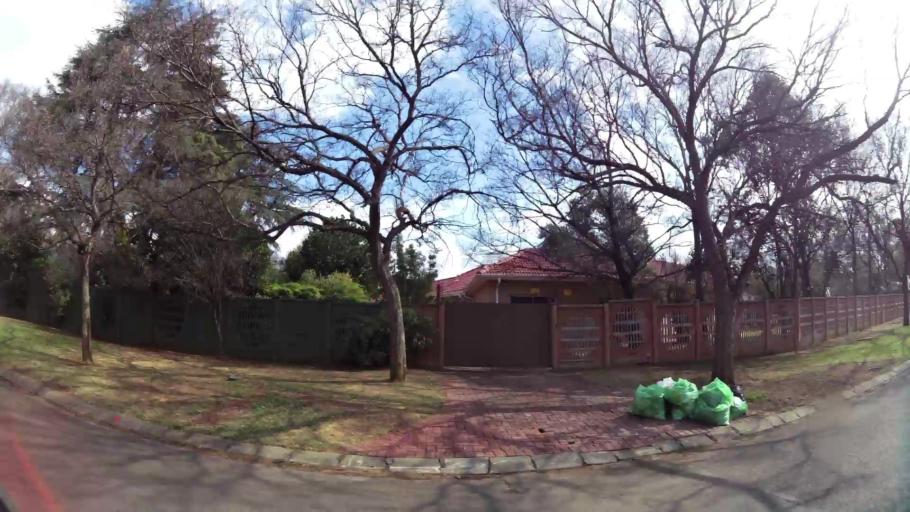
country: ZA
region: Gauteng
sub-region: Sedibeng District Municipality
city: Vanderbijlpark
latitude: -26.7390
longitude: 27.8365
